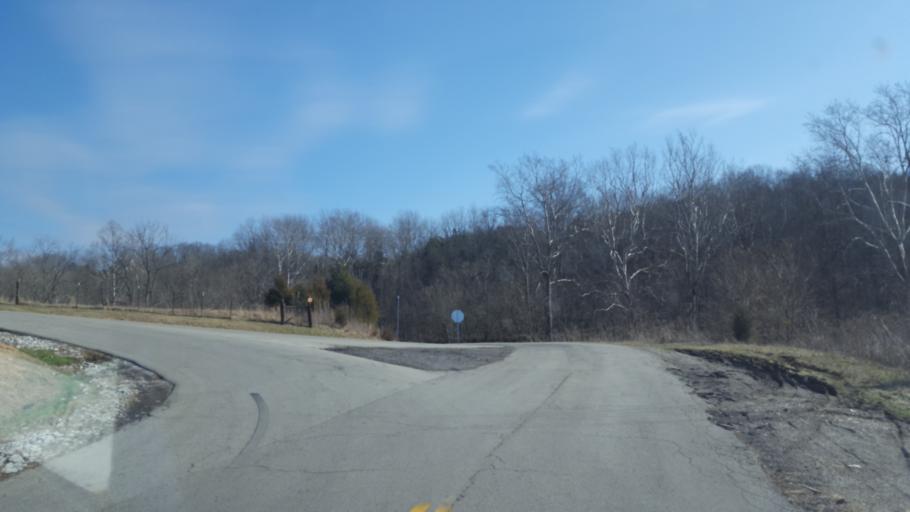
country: US
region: Kentucky
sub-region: Henry County
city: Eminence
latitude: 38.3015
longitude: -85.0468
